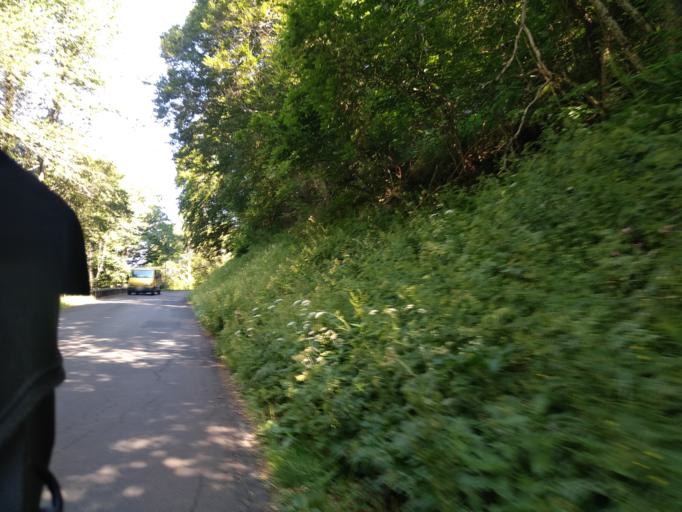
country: FR
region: Auvergne
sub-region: Departement du Puy-de-Dome
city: Mont-Dore
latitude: 45.5765
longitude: 2.8135
